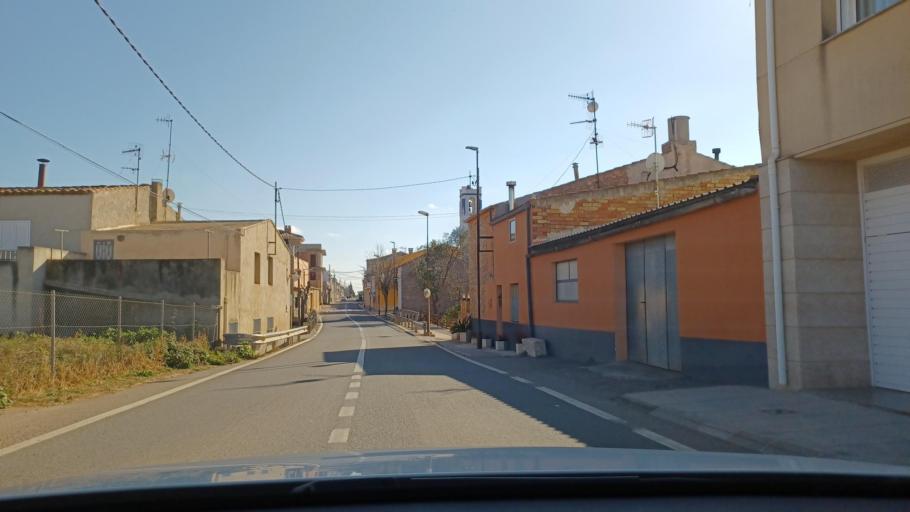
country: ES
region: Catalonia
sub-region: Provincia de Tarragona
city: Ulldecona
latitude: 40.6286
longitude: 0.3645
